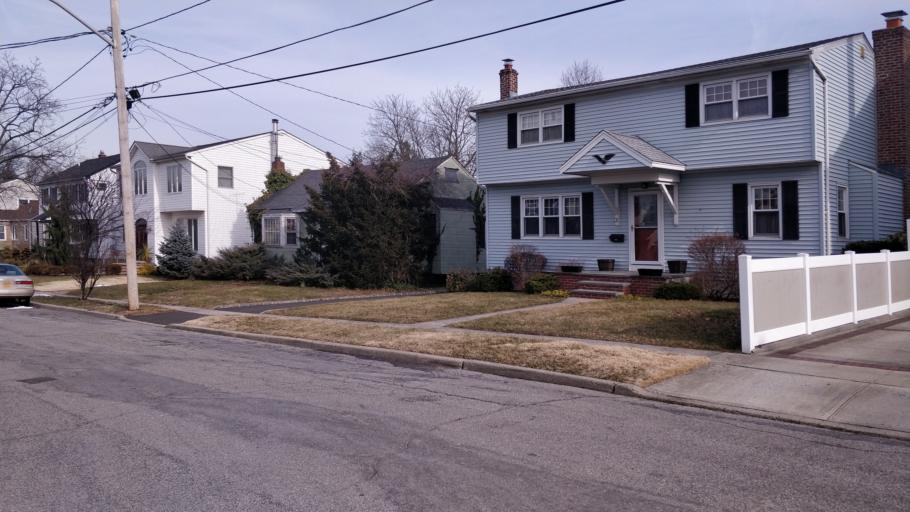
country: US
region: New York
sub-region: Nassau County
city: Hicksville
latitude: 40.7815
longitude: -73.5272
